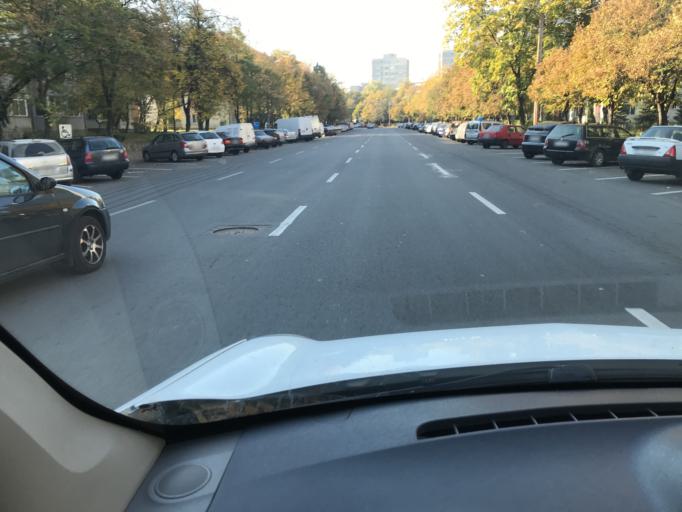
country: RO
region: Olt
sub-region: Municipiul Slatina
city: Slatina
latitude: 44.4353
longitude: 24.3701
